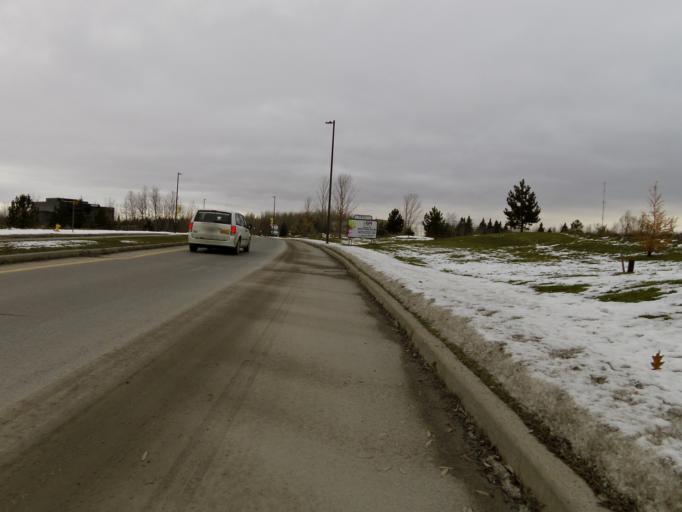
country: CA
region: Ontario
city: Bells Corners
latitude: 45.3467
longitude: -75.9017
